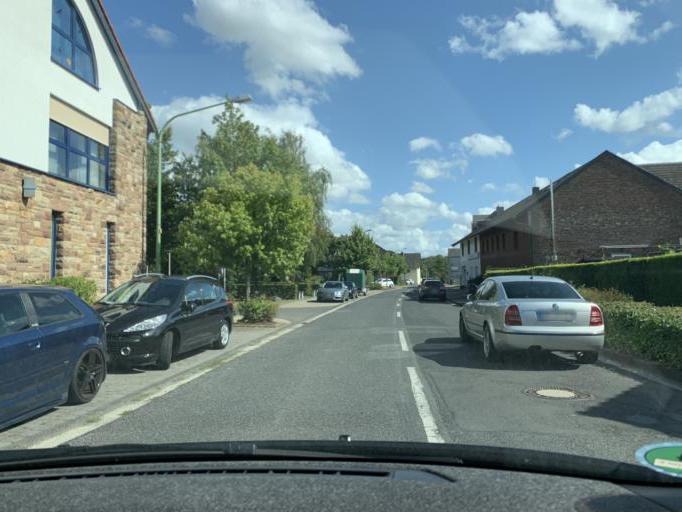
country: DE
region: North Rhine-Westphalia
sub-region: Regierungsbezirk Koln
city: Hurtgenwald
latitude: 50.7489
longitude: 6.4202
